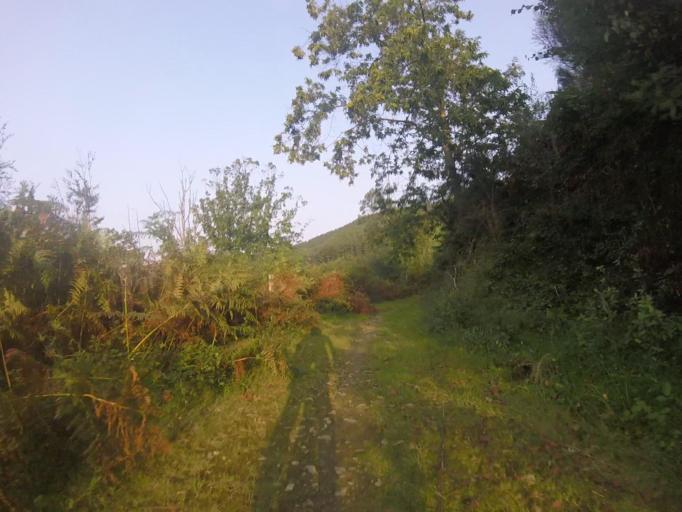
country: ES
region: Basque Country
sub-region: Provincia de Guipuzcoa
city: Errenteria
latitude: 43.2594
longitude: -1.8392
